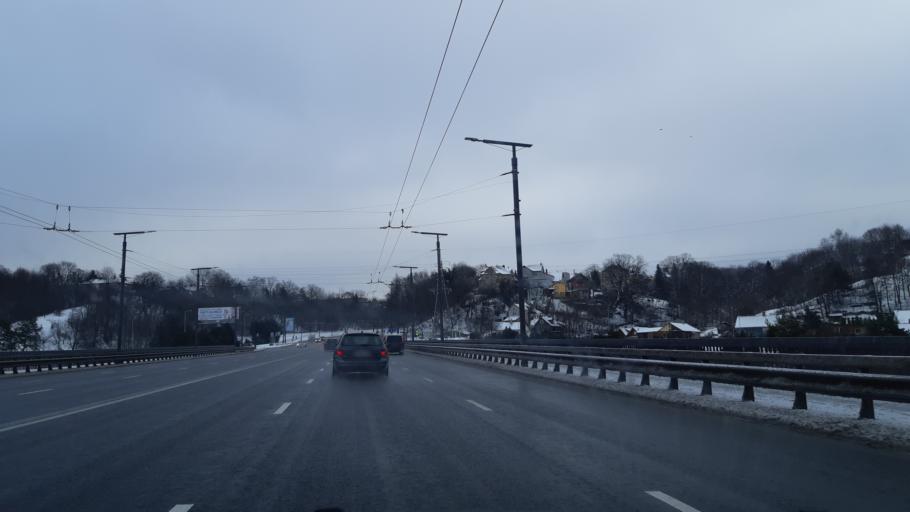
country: LT
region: Kauno apskritis
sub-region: Kaunas
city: Kaunas
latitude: 54.9143
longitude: 23.9101
